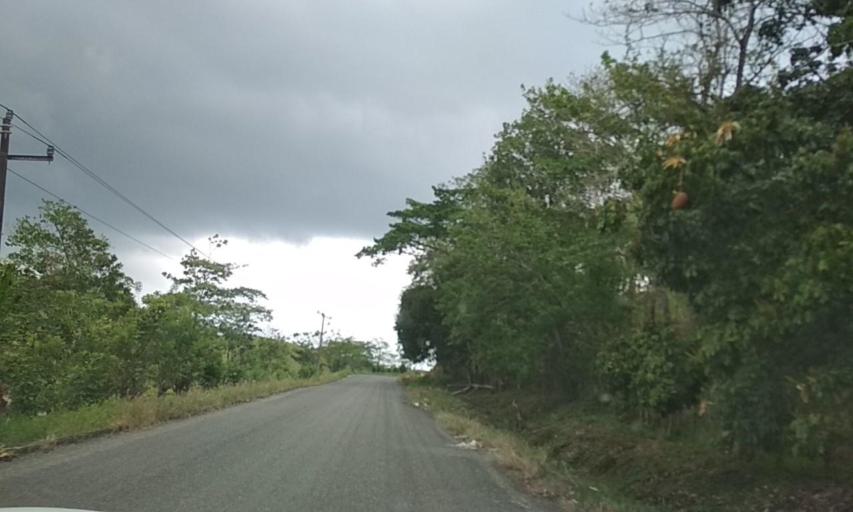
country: MX
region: Tabasco
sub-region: Huimanguillo
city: Francisco Rueda
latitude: 17.5451
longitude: -94.1288
